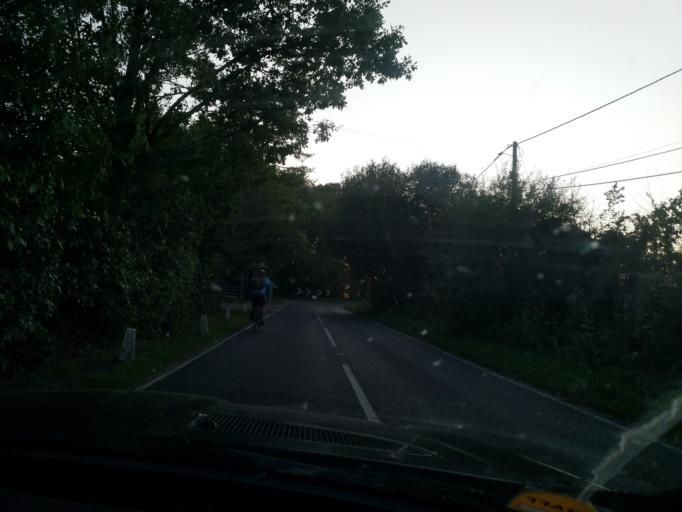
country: GB
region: England
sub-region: Kent
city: Sheerness
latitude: 51.4028
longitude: 0.8030
